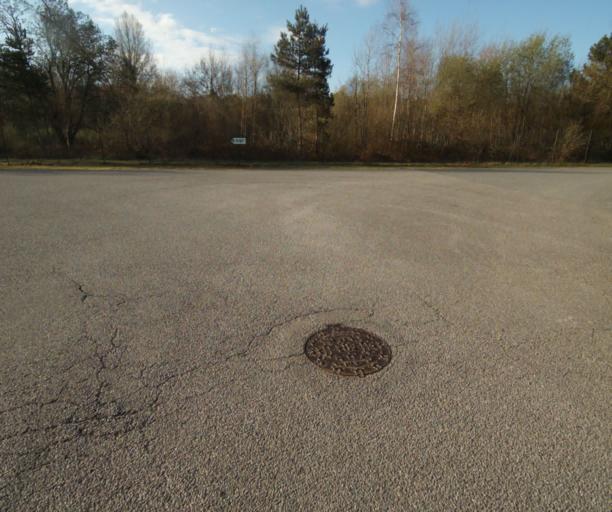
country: FR
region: Limousin
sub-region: Departement de la Correze
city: Correze
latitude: 45.3312
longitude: 1.8840
